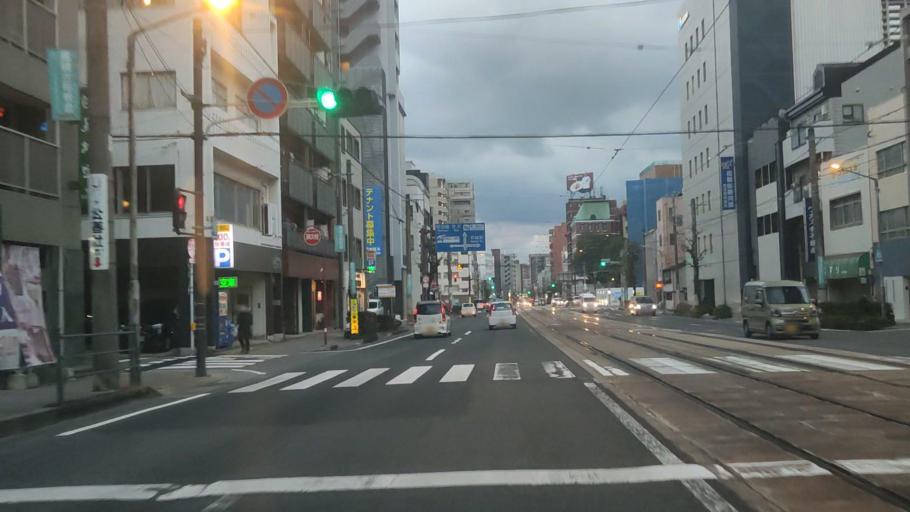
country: JP
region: Nagasaki
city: Nagasaki-shi
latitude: 32.7504
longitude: 129.8818
